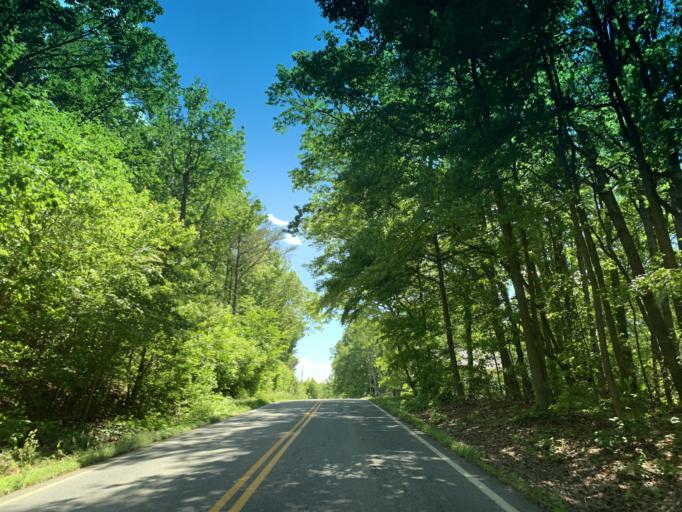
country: US
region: Maryland
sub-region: Cecil County
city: North East
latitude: 39.5619
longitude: -75.8904
